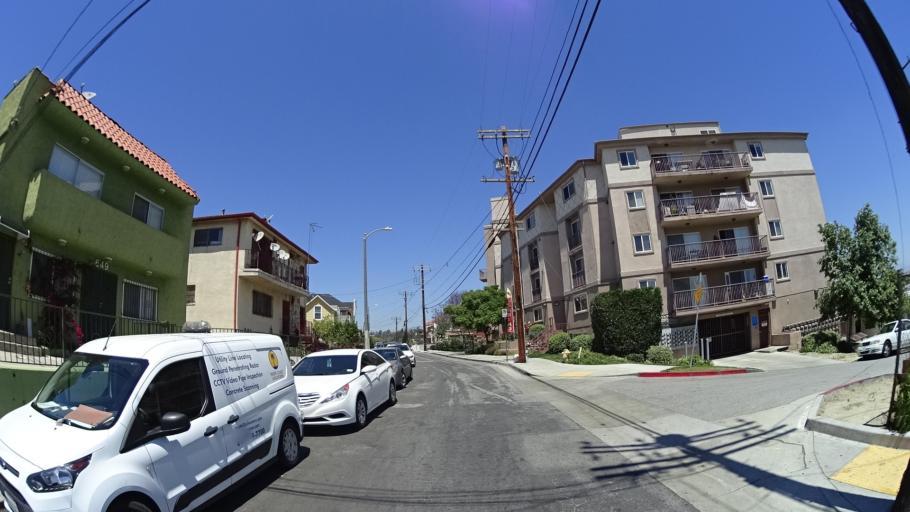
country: US
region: California
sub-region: Los Angeles County
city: Los Angeles
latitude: 34.0613
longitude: -118.2424
